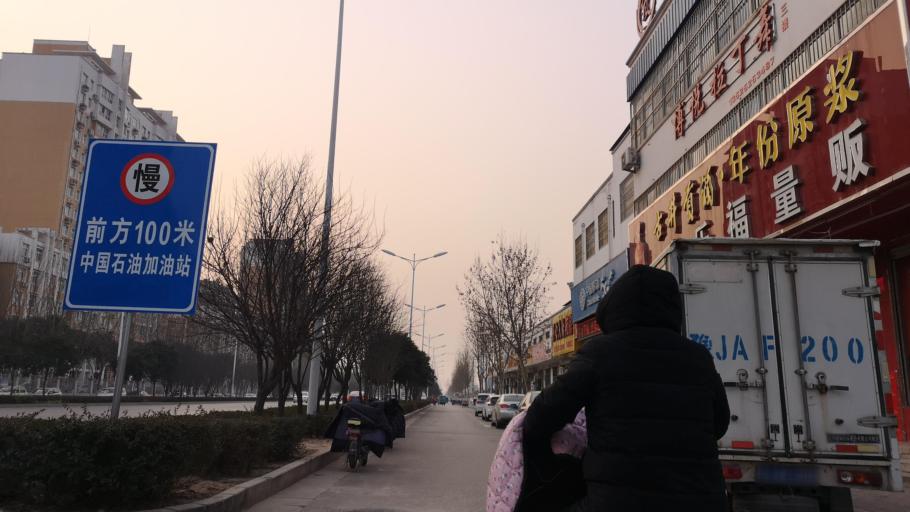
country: CN
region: Henan Sheng
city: Zhongyuanlu
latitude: 35.7893
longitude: 115.0870
